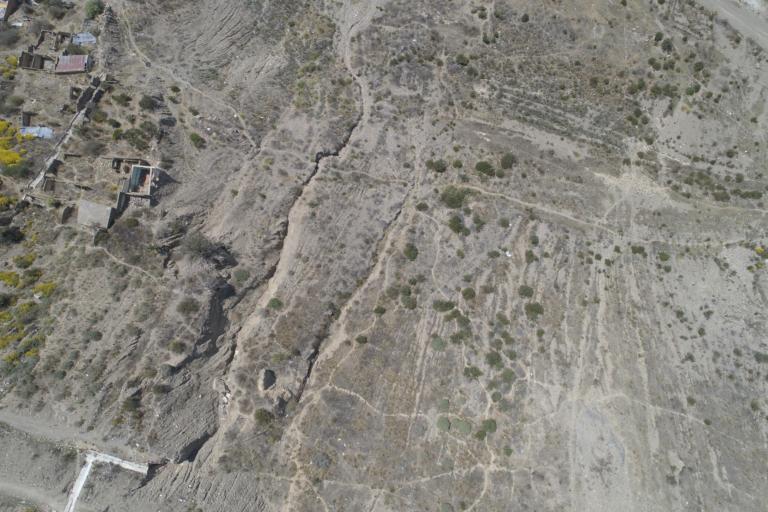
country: BO
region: La Paz
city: La Paz
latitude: -16.5019
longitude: -68.1002
